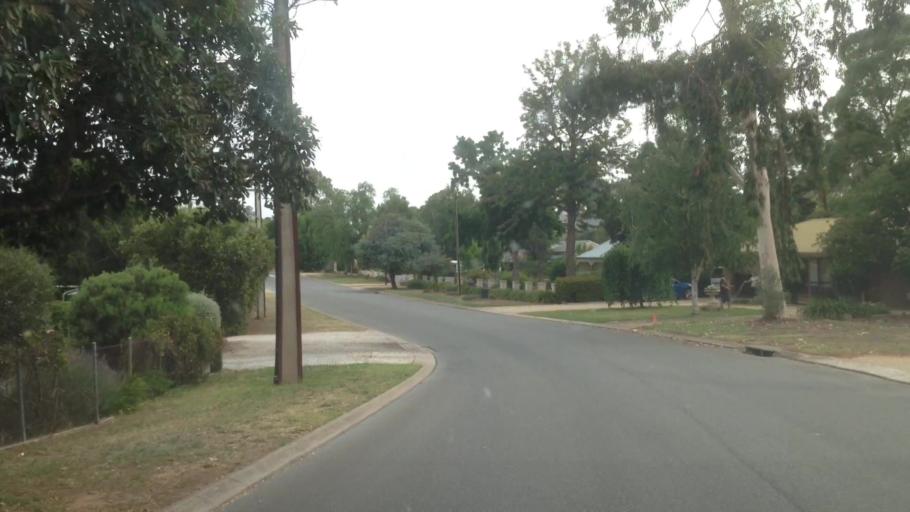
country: AU
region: South Australia
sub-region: Barossa
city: Williamstown
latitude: -34.6739
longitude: 138.8871
